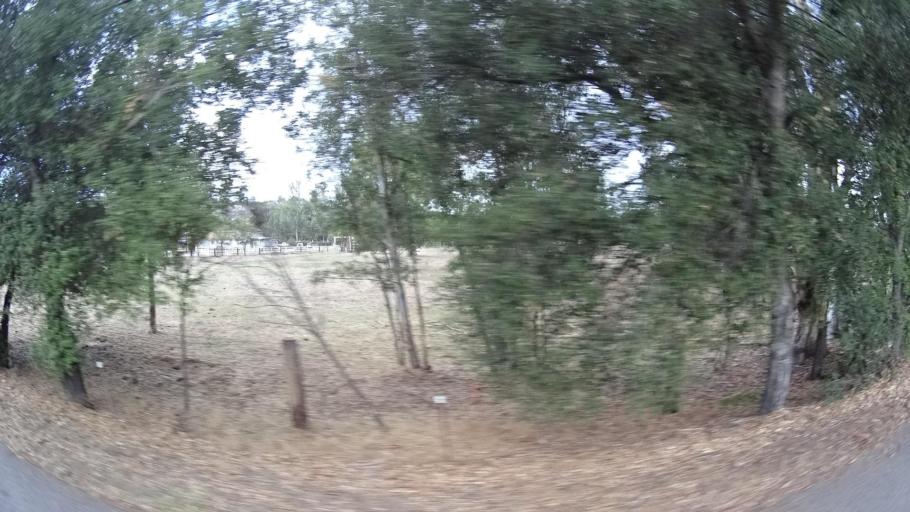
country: US
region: California
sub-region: San Diego County
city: Ramona
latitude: 33.0033
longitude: -116.9210
